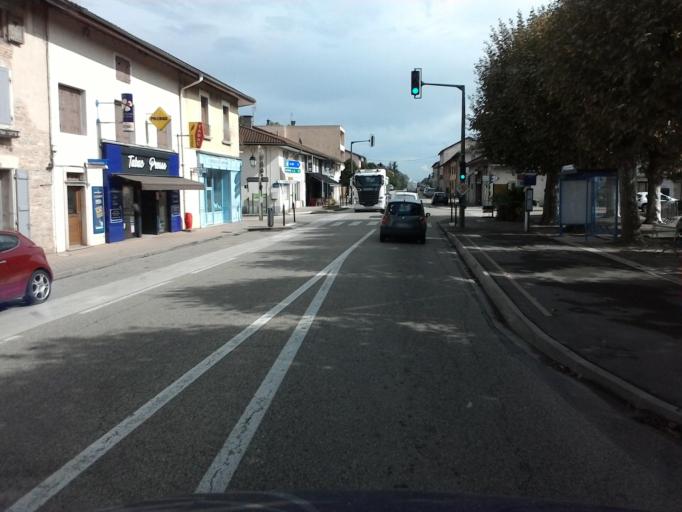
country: FR
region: Rhone-Alpes
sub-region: Departement de l'Ain
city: Polliat
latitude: 46.2493
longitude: 5.1259
